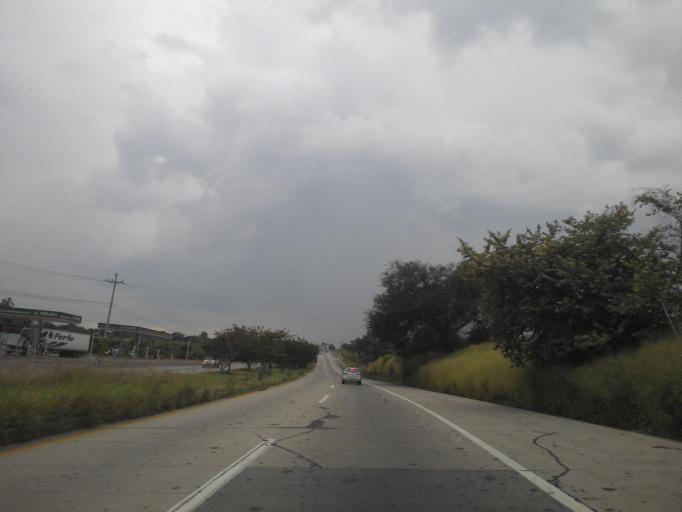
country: MX
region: Jalisco
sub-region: Tonala
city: Paseo Puente Viejo
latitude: 20.5758
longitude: -103.1802
